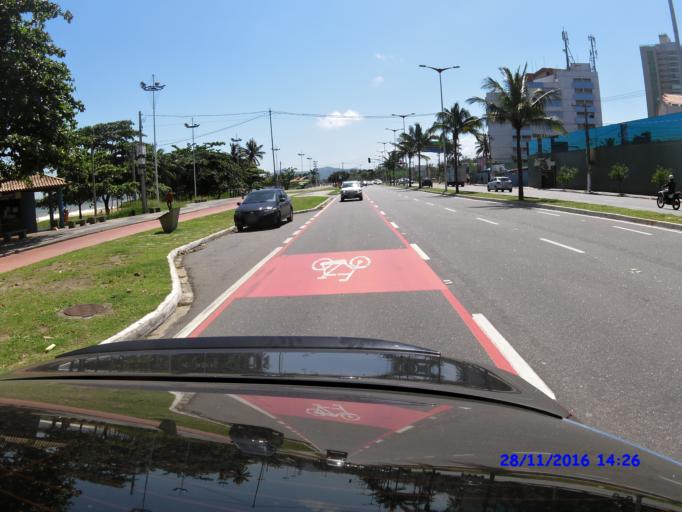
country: BR
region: Espirito Santo
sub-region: Vila Velha
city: Vila Velha
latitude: -20.2662
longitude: -40.2680
